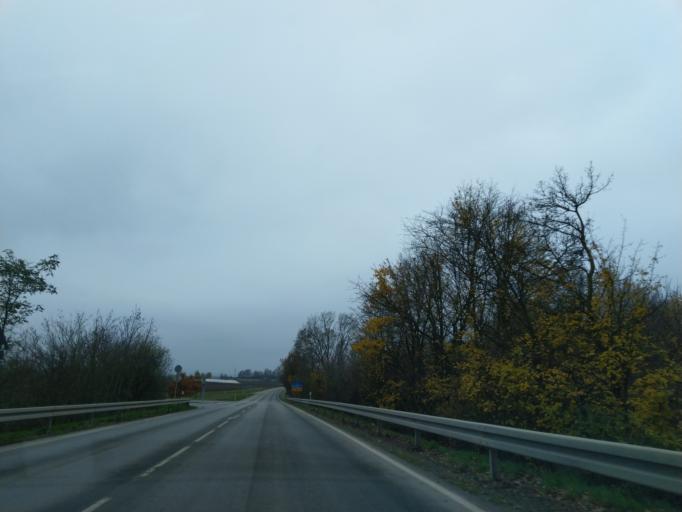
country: DE
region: Bavaria
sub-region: Lower Bavaria
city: Otzing
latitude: 48.7924
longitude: 12.8292
